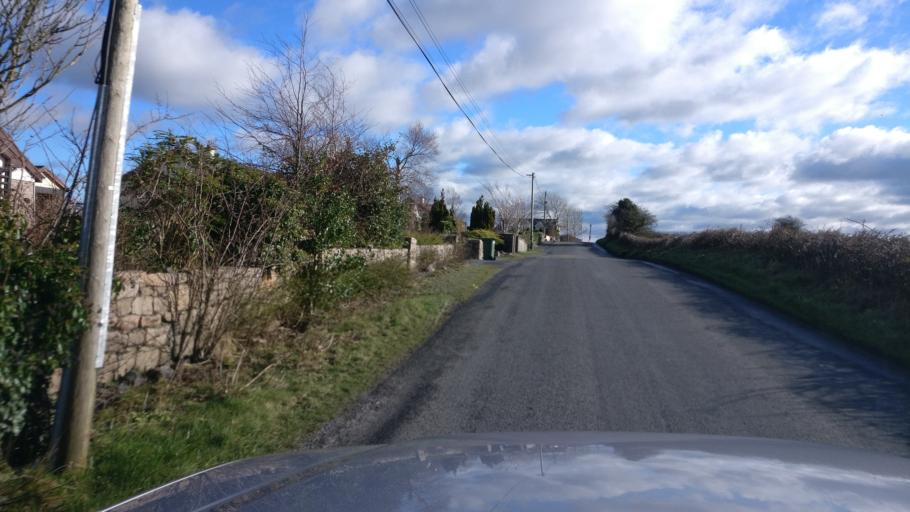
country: IE
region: Connaught
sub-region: County Galway
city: Oranmore
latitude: 53.2514
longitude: -8.8471
